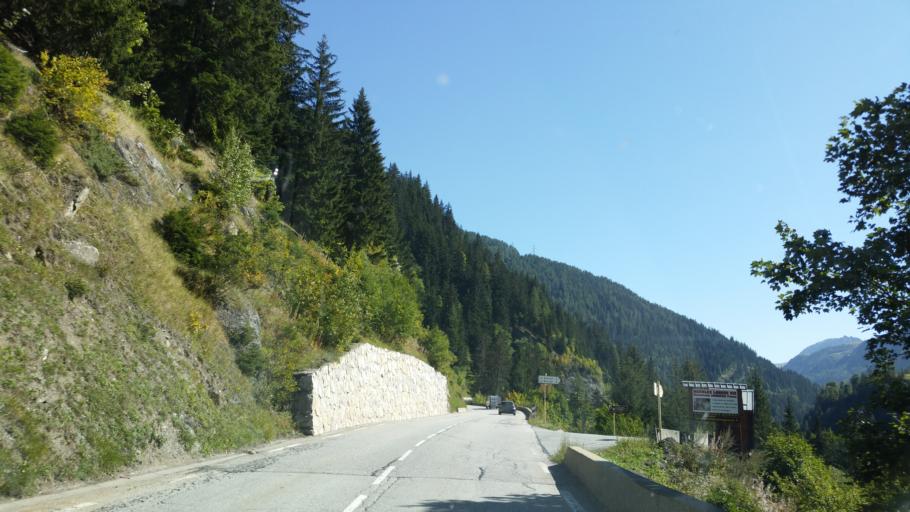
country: FR
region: Rhone-Alpes
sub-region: Departement de la Savoie
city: Tignes
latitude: 45.5434
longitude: 6.9090
